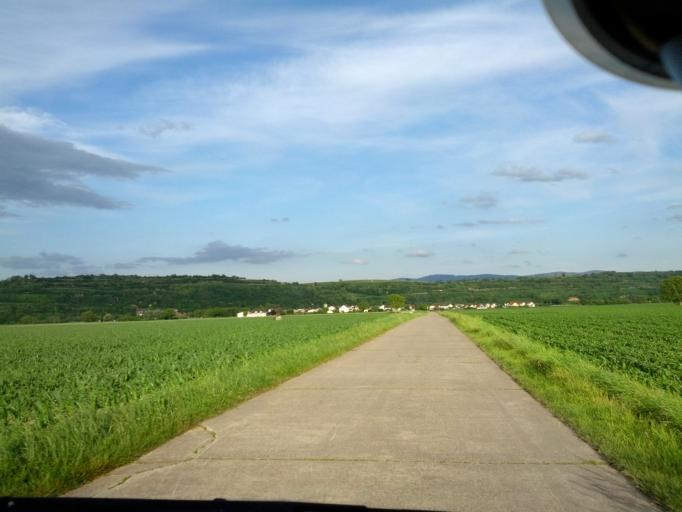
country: DE
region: Baden-Wuerttemberg
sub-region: Freiburg Region
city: Merdingen
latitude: 47.9888
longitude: 7.6537
